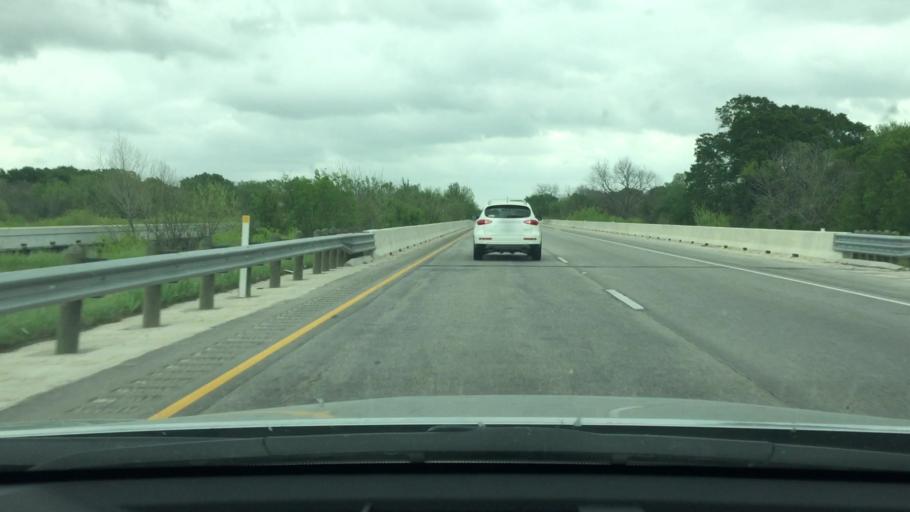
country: US
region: Texas
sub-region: Gonzales County
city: Waelder
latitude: 29.6924
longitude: -97.2360
